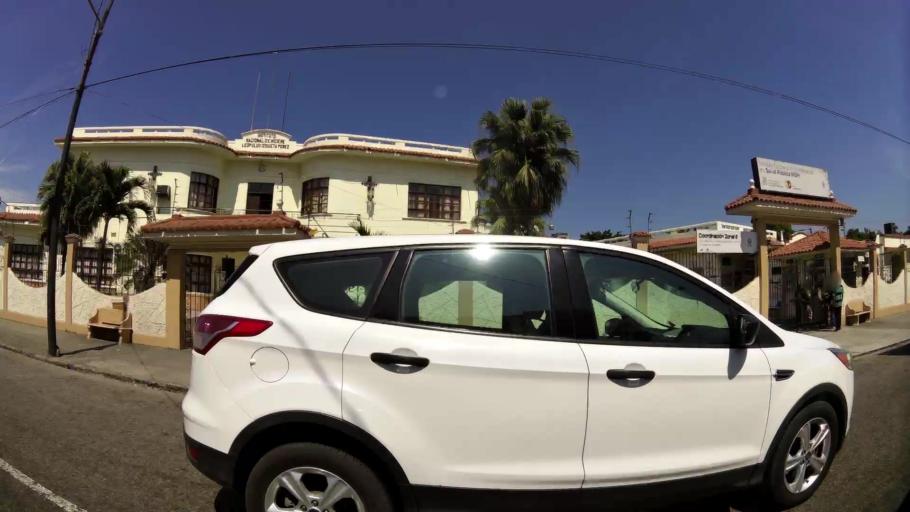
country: EC
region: Guayas
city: Guayaquil
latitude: -2.1823
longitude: -79.8913
